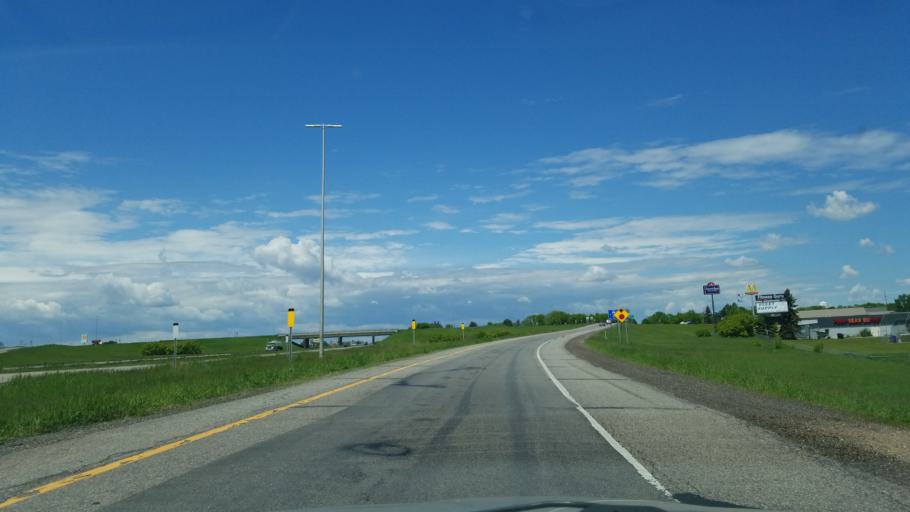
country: US
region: Minnesota
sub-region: Stearns County
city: Sauk Centre
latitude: 45.7193
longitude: -94.9477
